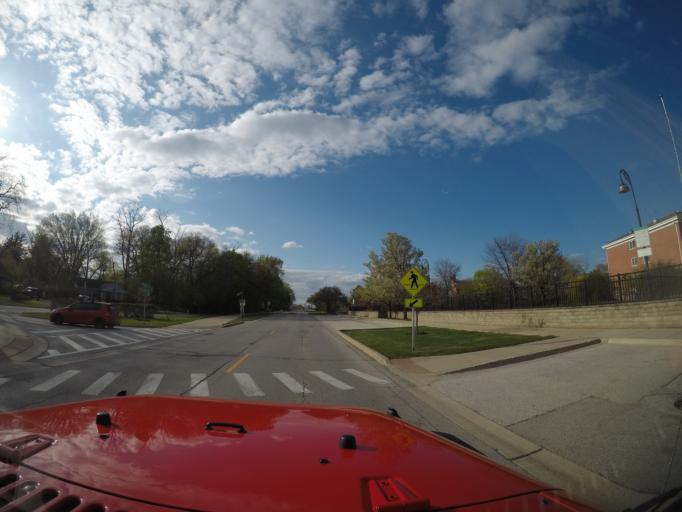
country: US
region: Illinois
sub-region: Cook County
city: Glenview
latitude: 42.0761
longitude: -87.8067
